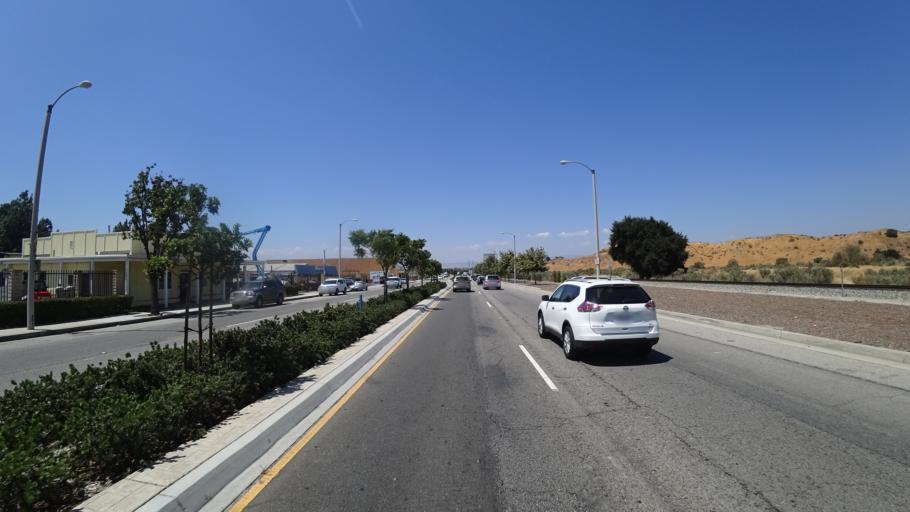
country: US
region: California
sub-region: Los Angeles County
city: Santa Clarita
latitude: 34.3889
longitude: -118.5344
